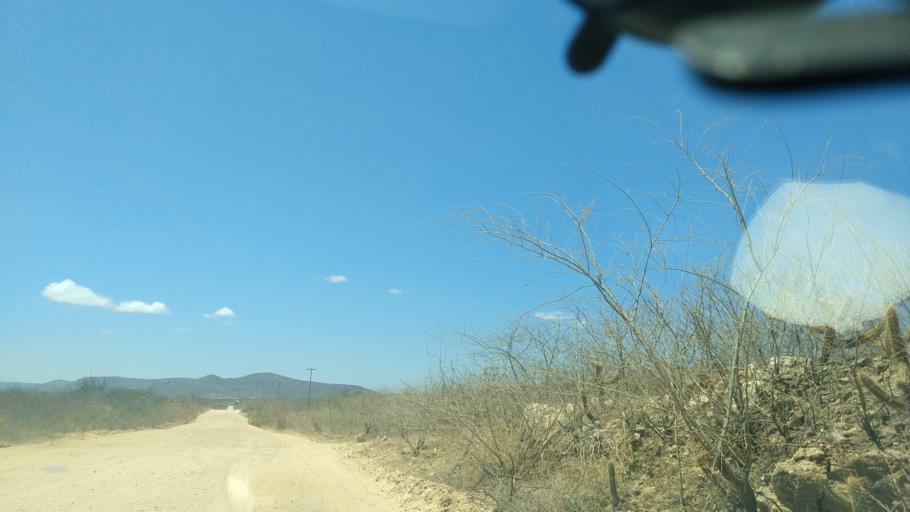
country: BR
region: Rio Grande do Norte
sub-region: Sao Tome
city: Sao Tome
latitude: -5.9726
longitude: -36.1650
